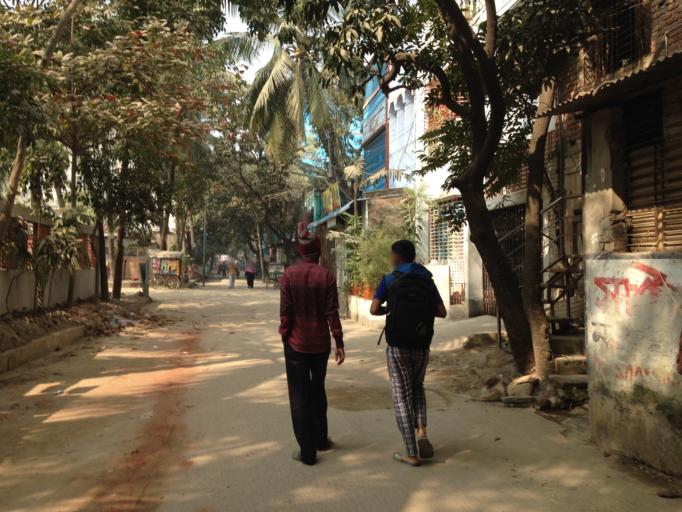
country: BD
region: Dhaka
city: Azimpur
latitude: 23.8073
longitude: 90.3804
